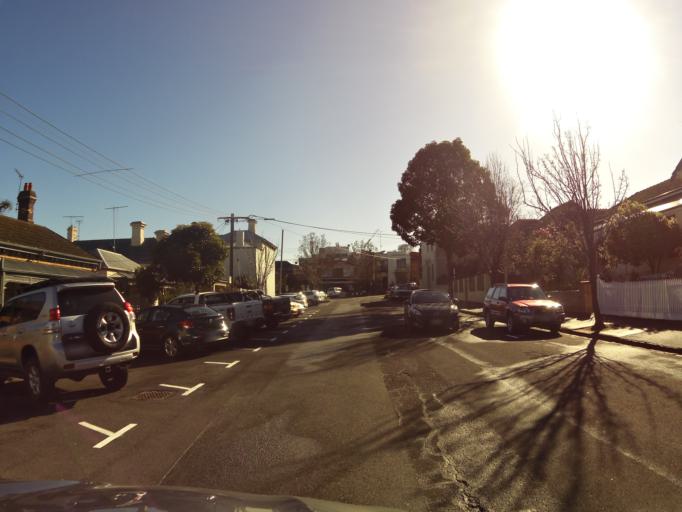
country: AU
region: Victoria
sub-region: Yarra
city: Richmond
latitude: -37.8228
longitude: 144.9949
